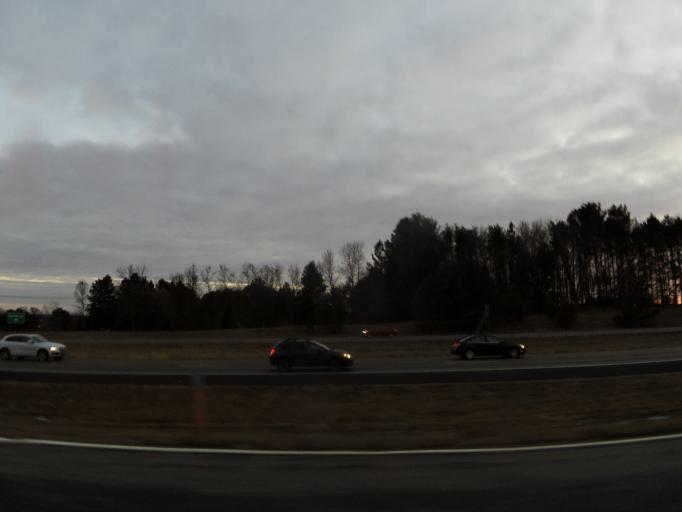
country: US
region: Minnesota
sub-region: Washington County
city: Lake Elmo
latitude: 45.0361
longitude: -92.8711
